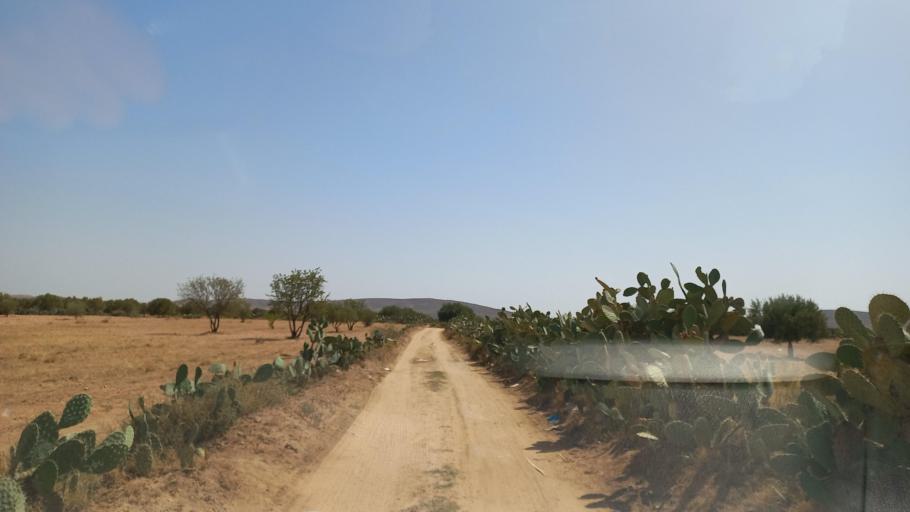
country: TN
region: Al Qasrayn
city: Kasserine
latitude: 35.2186
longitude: 9.0363
